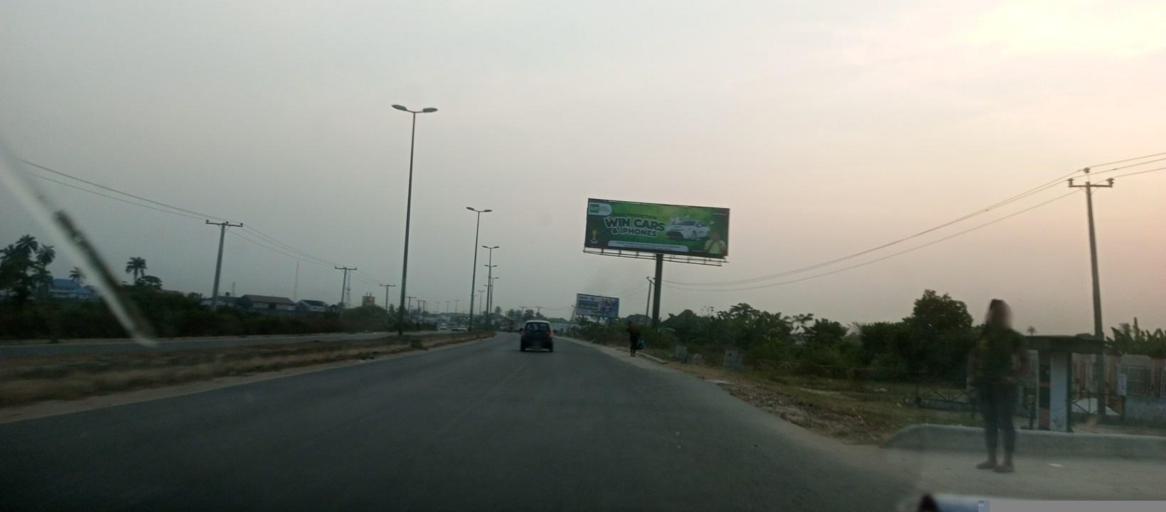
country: NG
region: Rivers
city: Emuoha
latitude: 4.9264
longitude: 6.9988
